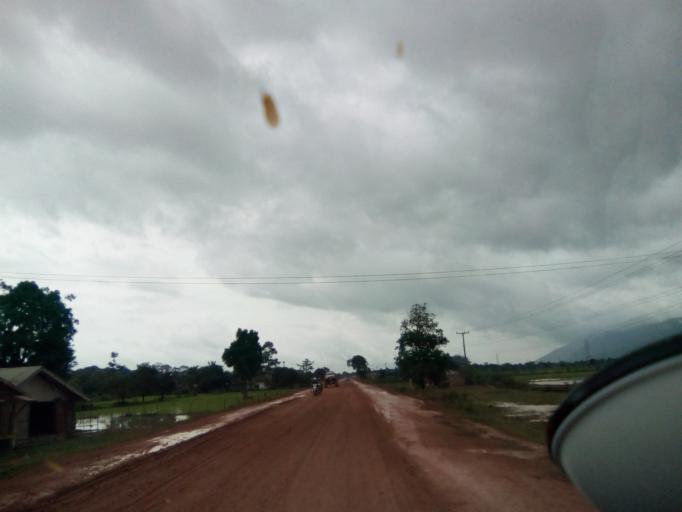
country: LA
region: Attapu
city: Attapu
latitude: 14.7582
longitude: 106.7091
